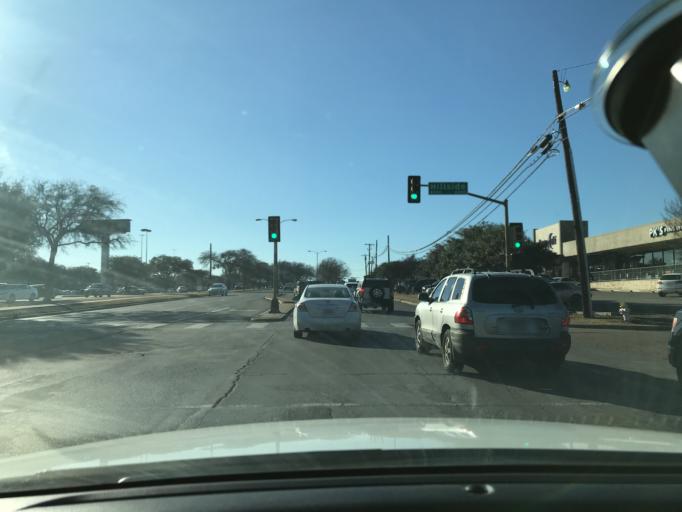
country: US
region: Texas
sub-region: Dallas County
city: Highland Park
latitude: 32.8367
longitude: -96.7494
